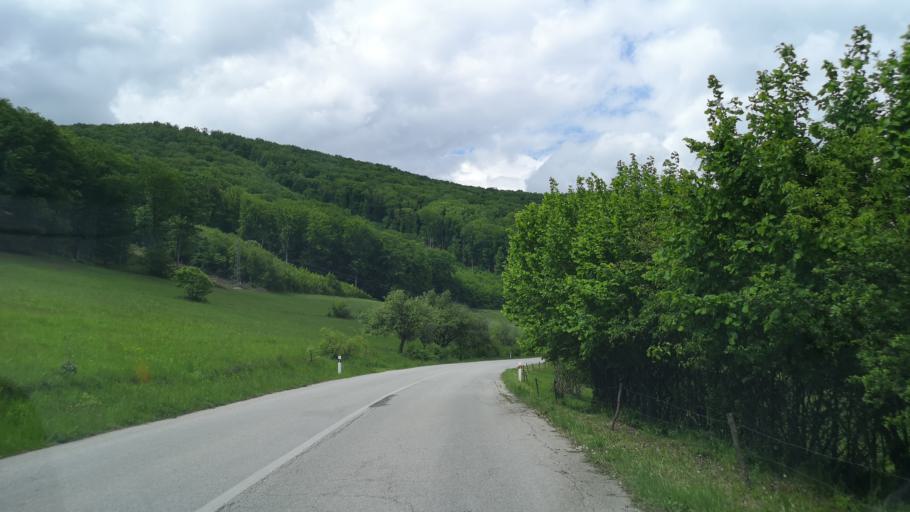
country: SK
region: Kosicky
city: Roznava
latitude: 48.6398
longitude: 20.3585
